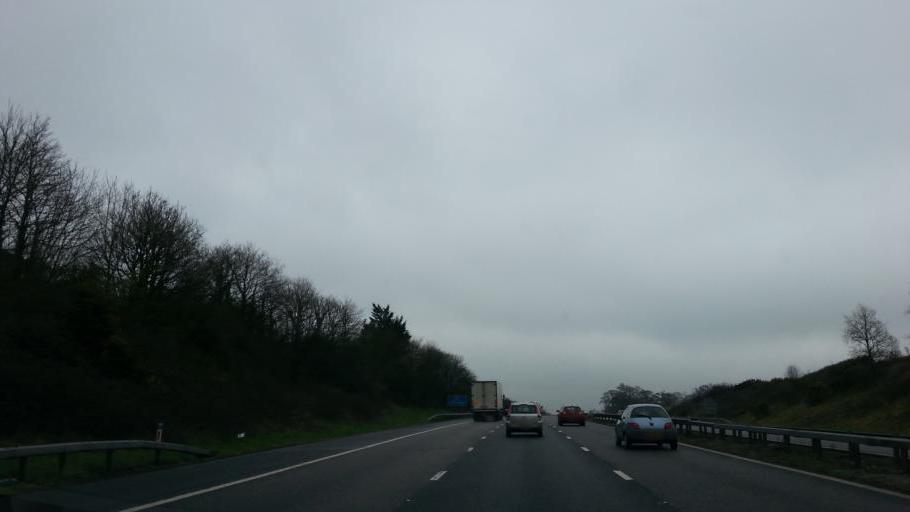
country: GB
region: England
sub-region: Devon
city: Uffculme
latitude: 50.9489
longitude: -3.2753
